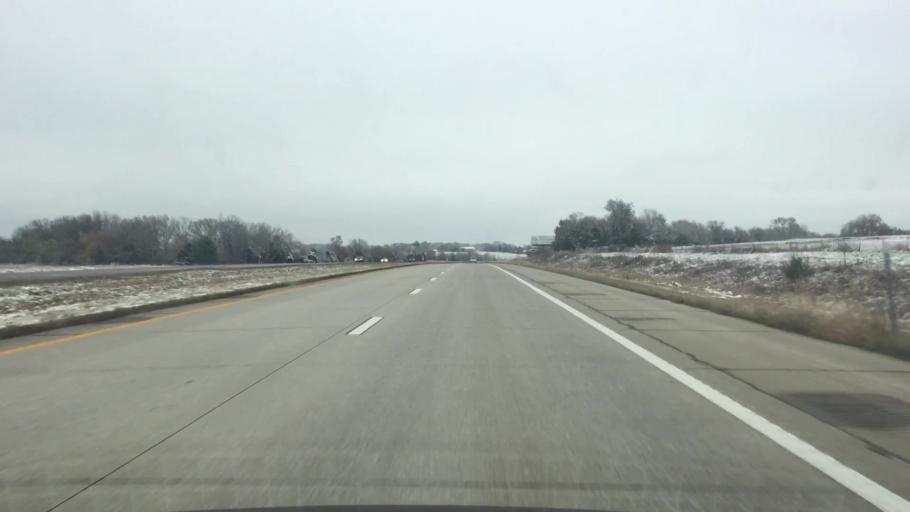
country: US
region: Missouri
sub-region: Saint Clair County
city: Osceola
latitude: 38.1815
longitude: -93.7293
